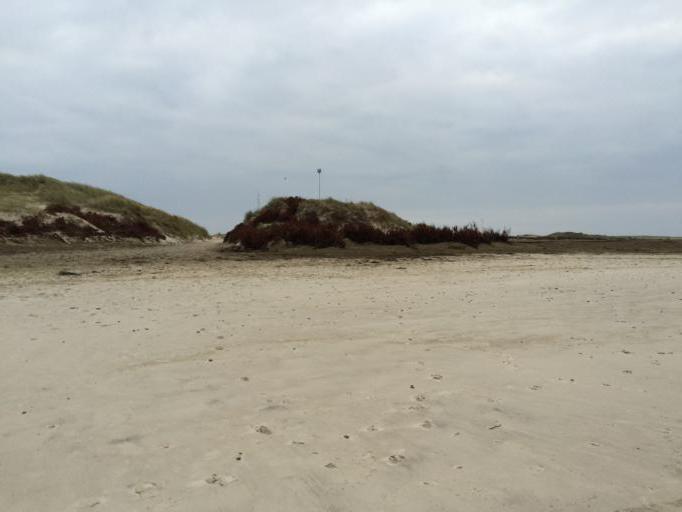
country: DK
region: Central Jutland
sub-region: Holstebro Kommune
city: Ulfborg
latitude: 56.3732
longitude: 8.1163
